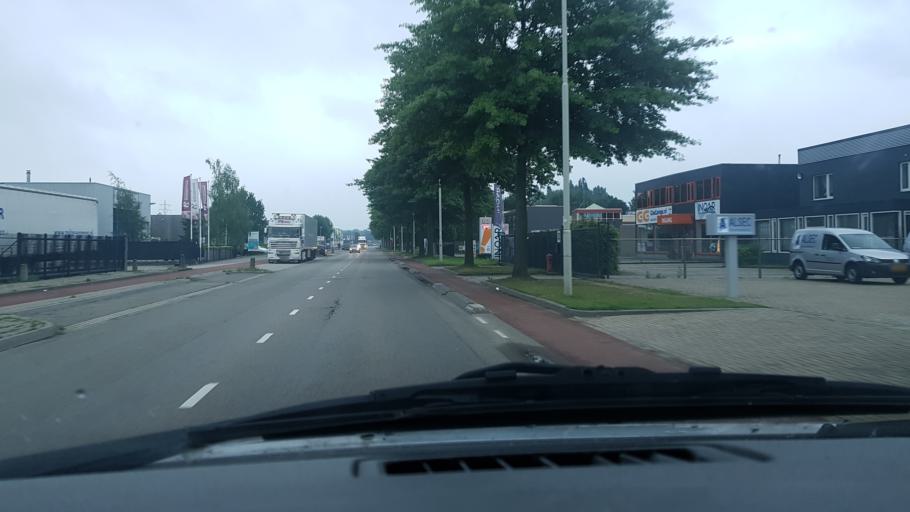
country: NL
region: Gelderland
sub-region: Gemeente Nijmegen
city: Lindenholt
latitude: 51.8454
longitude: 5.8004
